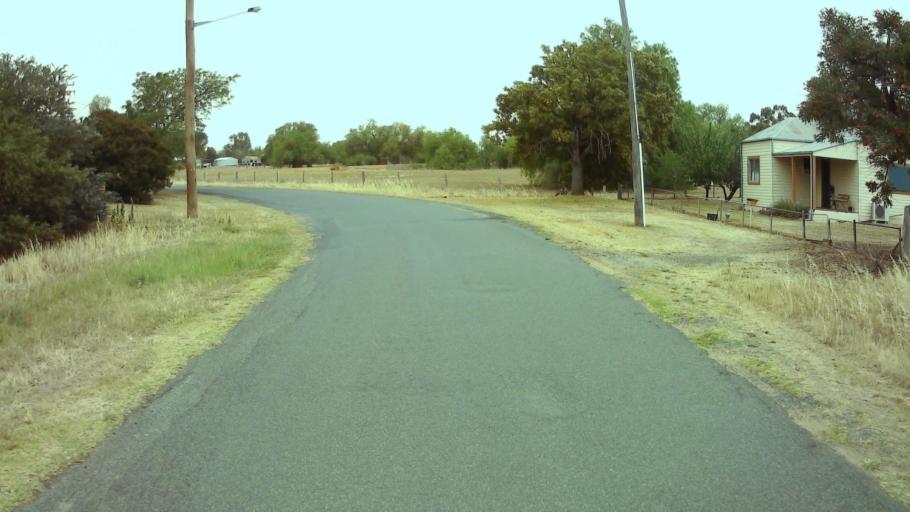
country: AU
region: New South Wales
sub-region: Weddin
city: Grenfell
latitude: -33.8995
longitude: 148.1674
